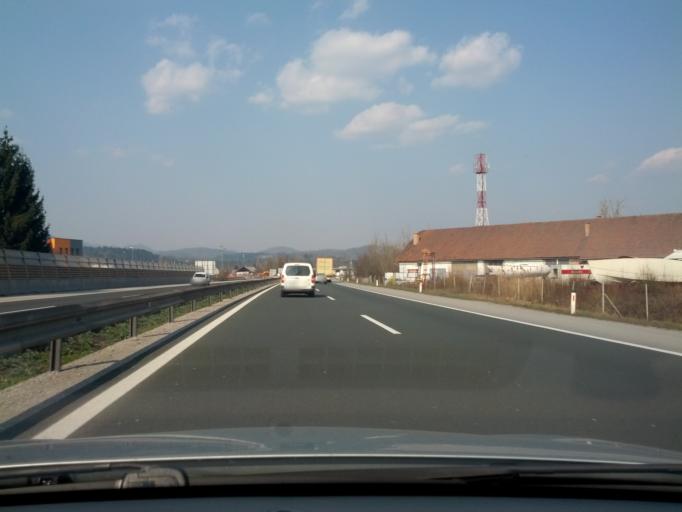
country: SI
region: Vrhnika
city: Vrhnika
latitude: 45.9729
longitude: 14.3064
